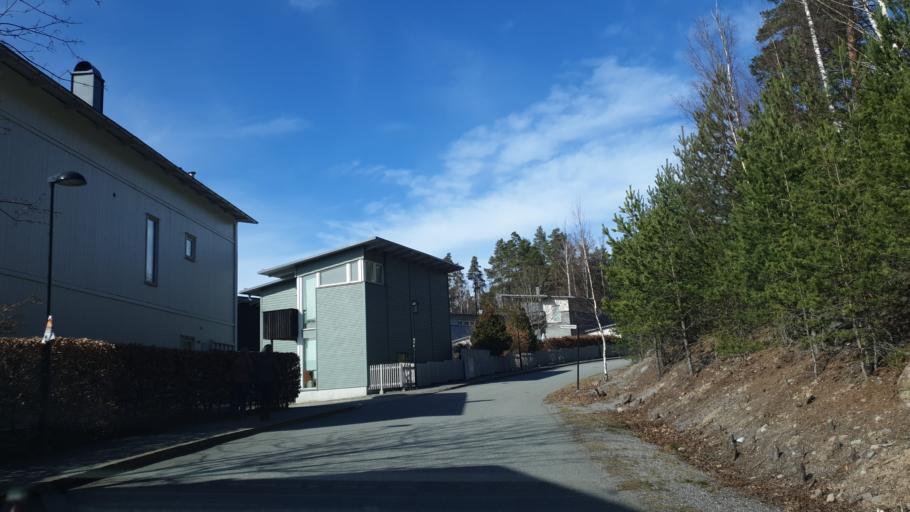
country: SE
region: Stockholm
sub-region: Solna Kommun
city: Rasunda
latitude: 59.4018
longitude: 17.9911
